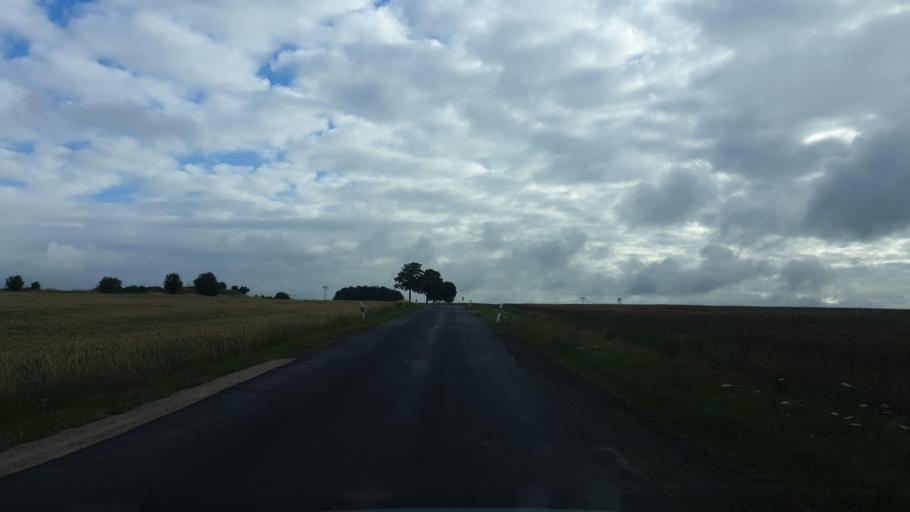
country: DE
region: Saxony
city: Limbach
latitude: 50.5823
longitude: 12.2279
